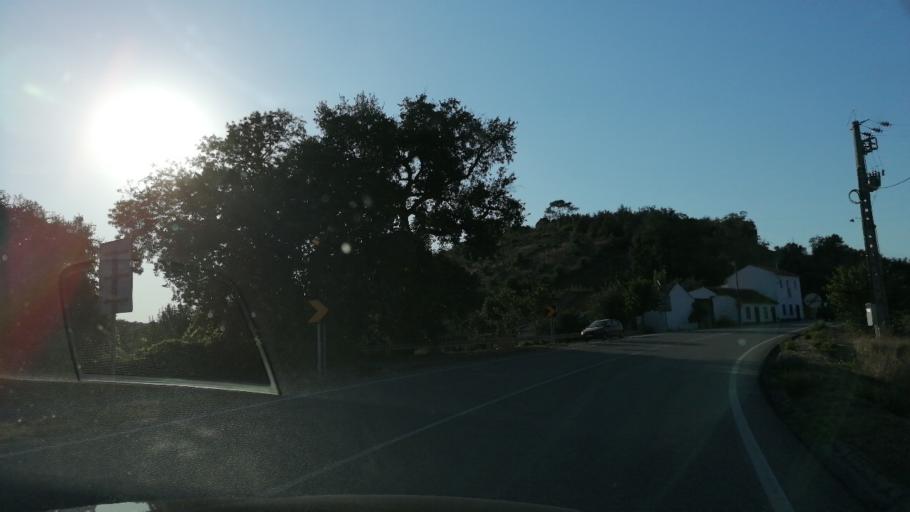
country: PT
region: Santarem
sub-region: Alcanena
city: Alcanena
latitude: 39.3661
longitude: -8.6562
